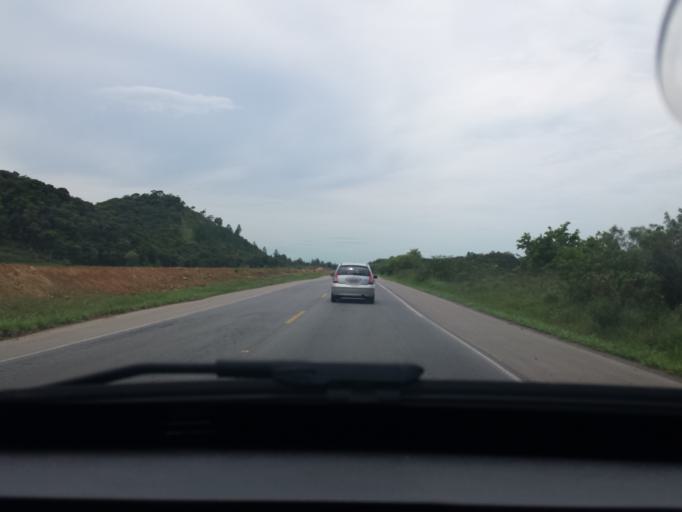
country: BR
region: Santa Catarina
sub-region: Gaspar
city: Gaspar
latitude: -26.8814
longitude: -48.8522
